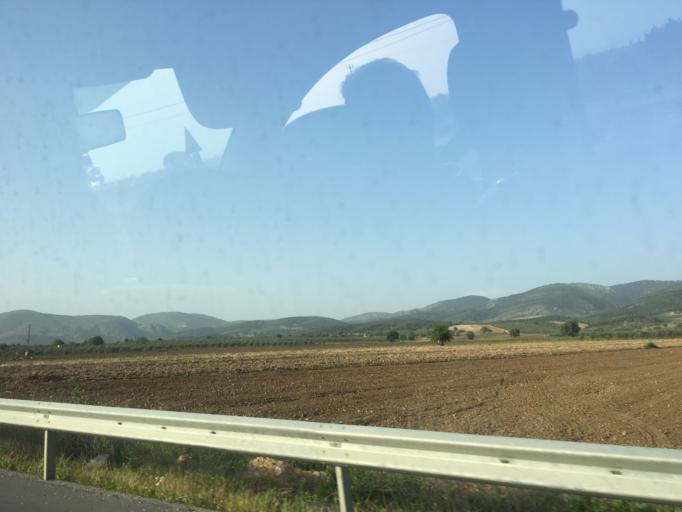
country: TR
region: Manisa
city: Golmarmara
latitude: 38.7925
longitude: 27.8997
